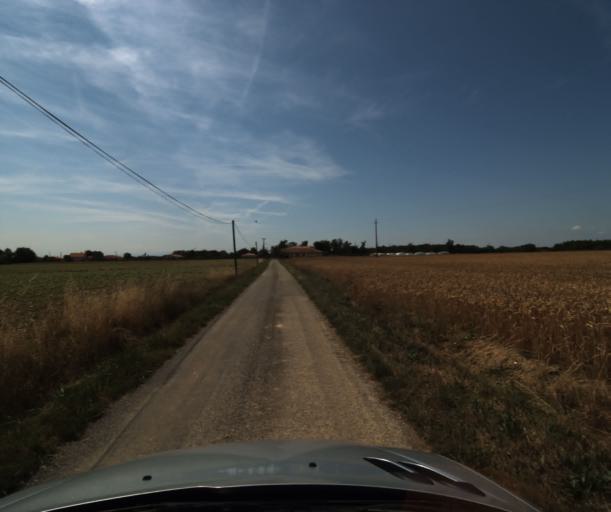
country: FR
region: Midi-Pyrenees
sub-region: Departement de la Haute-Garonne
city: Lherm
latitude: 43.4540
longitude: 1.1868
